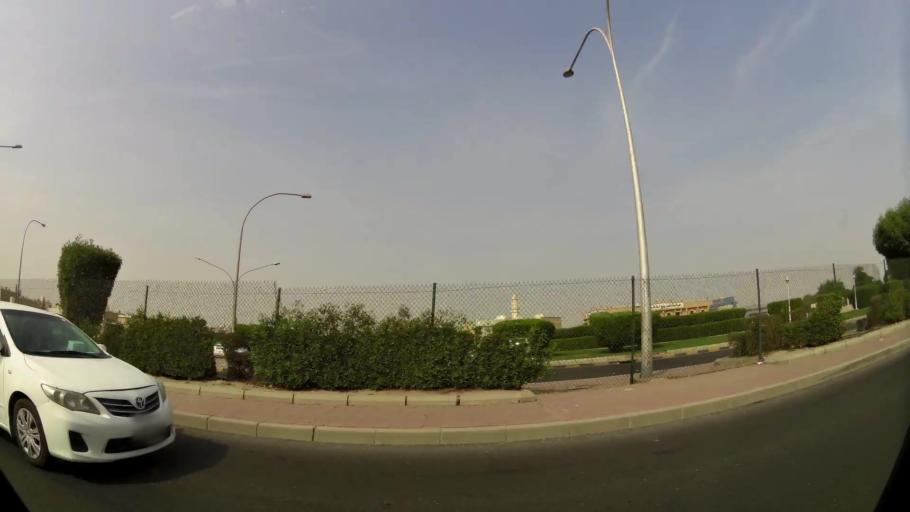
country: KW
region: Al Asimah
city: Ar Rabiyah
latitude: 29.2889
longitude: 47.9399
